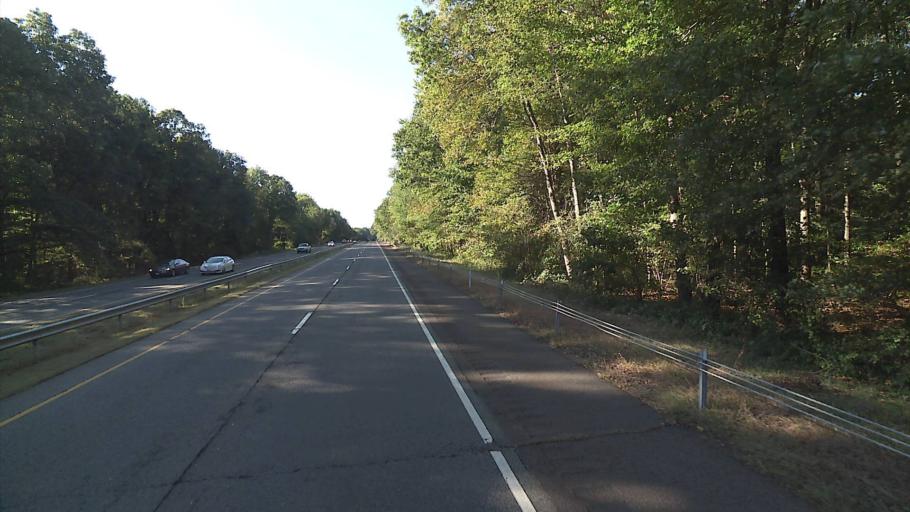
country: US
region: Connecticut
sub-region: New Haven County
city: North Haven
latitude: 41.4225
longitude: -72.8549
